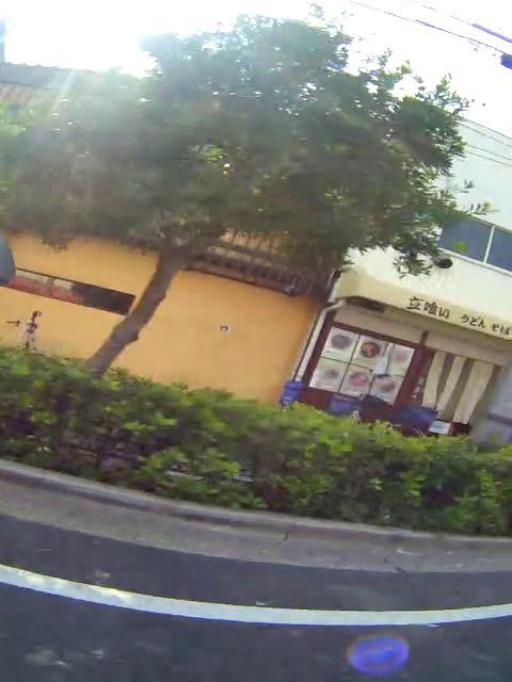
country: JP
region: Osaka
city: Osaka-shi
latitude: 34.6919
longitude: 135.5460
